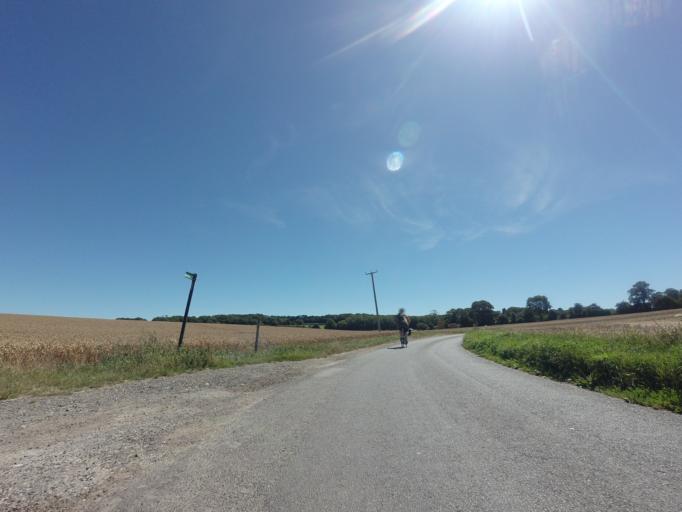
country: GB
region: England
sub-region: Kent
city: Deal
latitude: 51.1932
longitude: 1.3654
